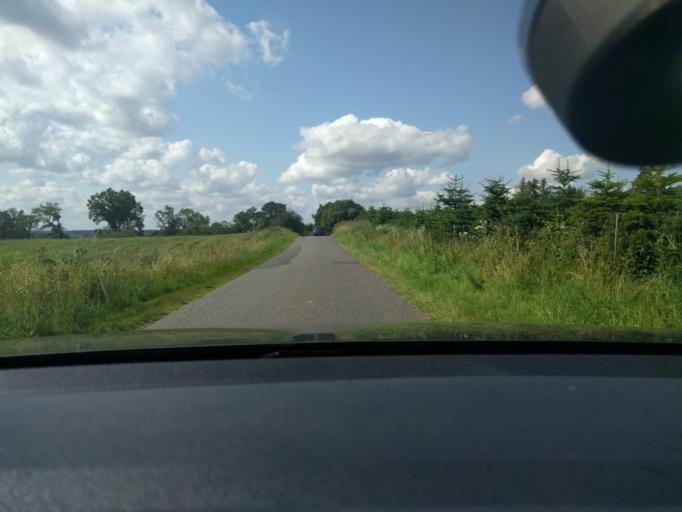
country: DK
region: Central Jutland
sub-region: Viborg Kommune
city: Bjerringbro
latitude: 56.4665
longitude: 9.5976
